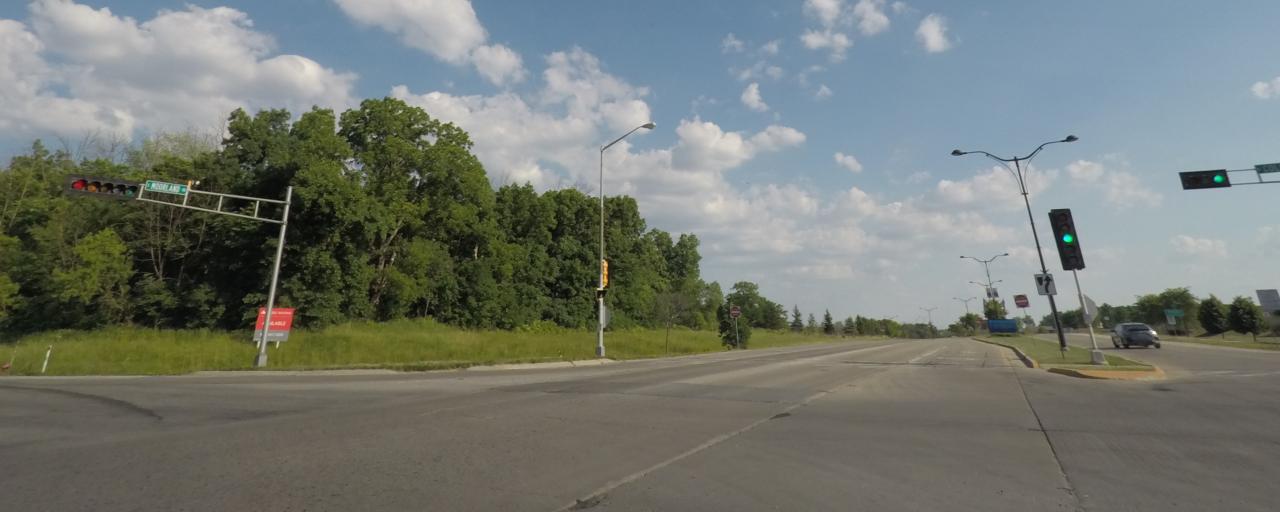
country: US
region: Wisconsin
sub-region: Waukesha County
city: Muskego
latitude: 42.9301
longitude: -88.1140
